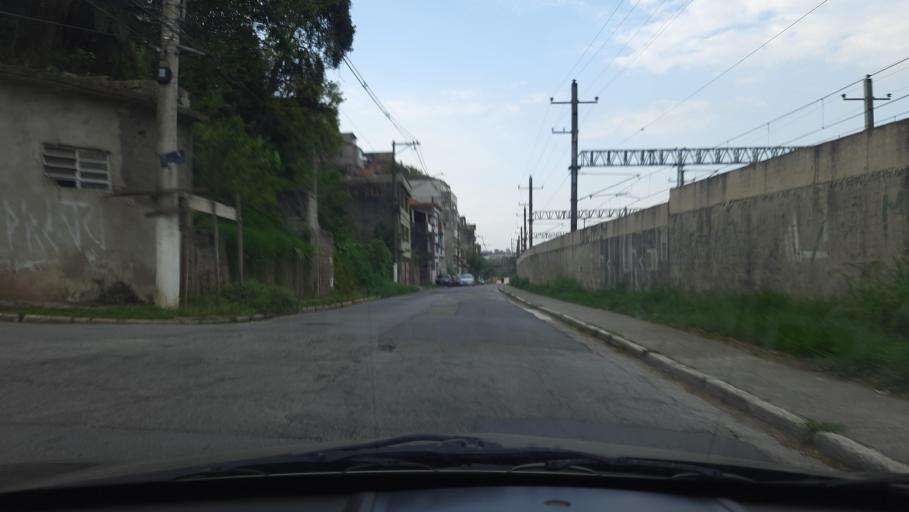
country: BR
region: Sao Paulo
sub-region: Caieiras
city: Caieiras
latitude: -23.4508
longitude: -46.7426
